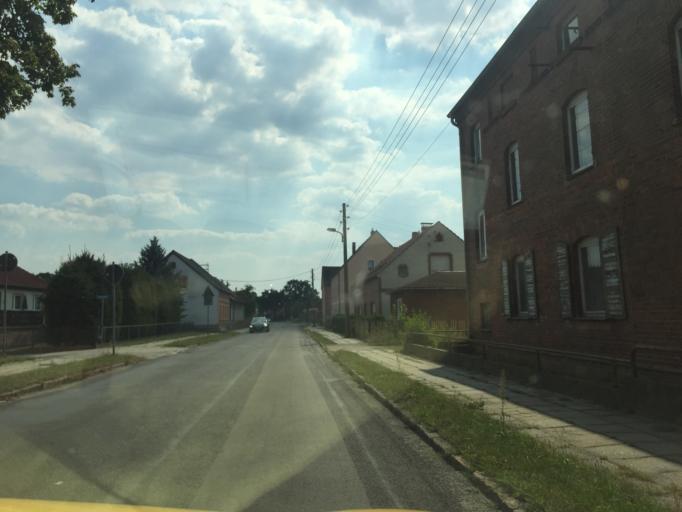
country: DE
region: Brandenburg
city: Welzow
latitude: 51.5741
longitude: 14.1730
